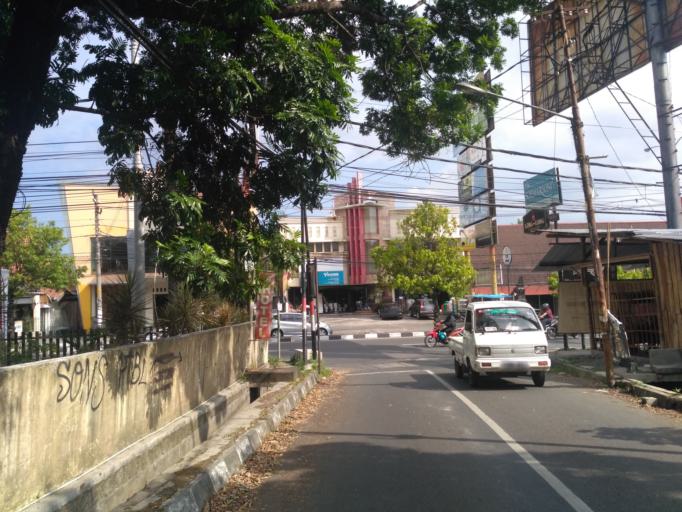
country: ID
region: Daerah Istimewa Yogyakarta
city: Depok
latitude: -7.7830
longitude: 110.4052
